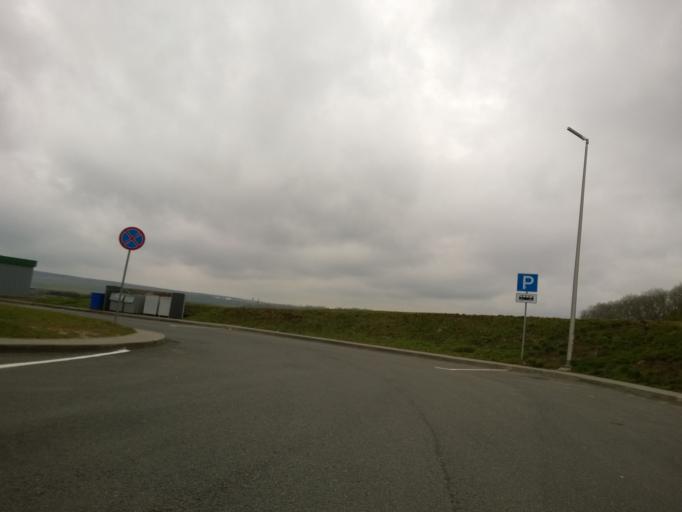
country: BY
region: Minsk
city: Slabada
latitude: 54.0226
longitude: 27.9304
